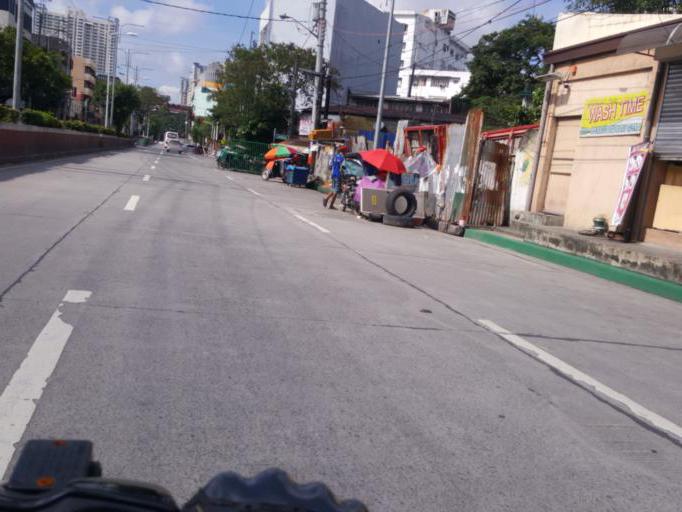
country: PH
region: Metro Manila
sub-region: City of Manila
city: Manila
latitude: 14.6129
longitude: 120.9864
